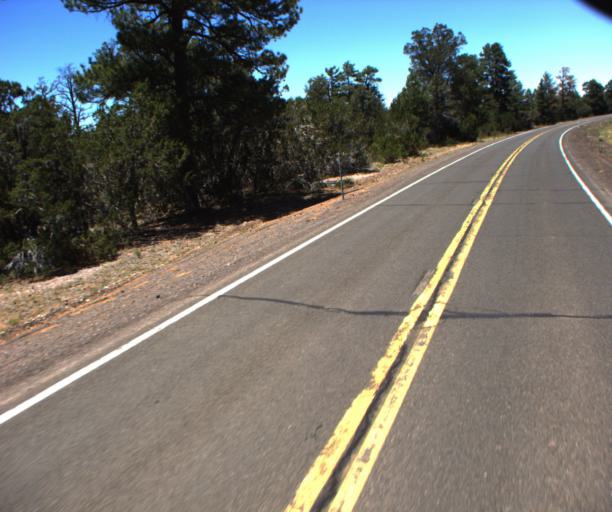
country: US
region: Arizona
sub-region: Gila County
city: Star Valley
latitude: 34.6736
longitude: -111.1103
